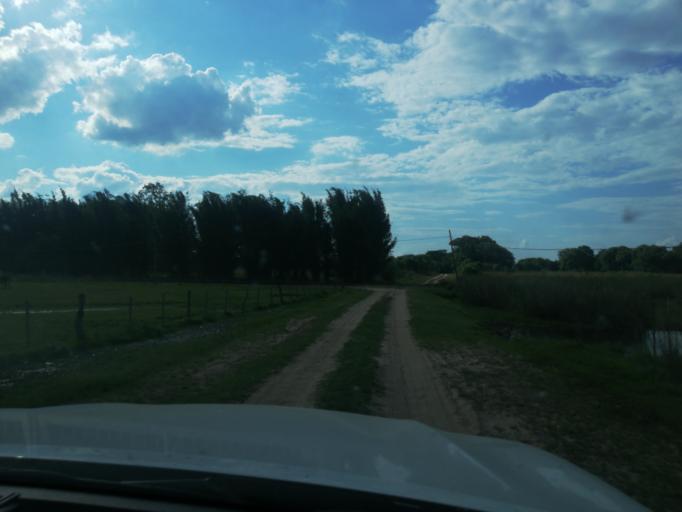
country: AR
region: Corrientes
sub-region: Departamento de San Miguel
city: San Miguel
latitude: -27.9929
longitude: -57.5754
